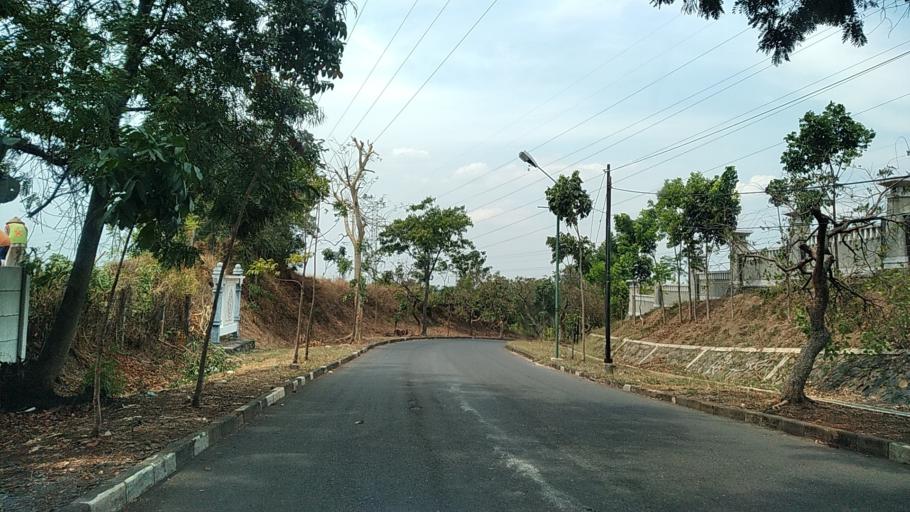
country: ID
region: Central Java
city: Semarang
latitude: -7.0476
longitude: 110.4348
